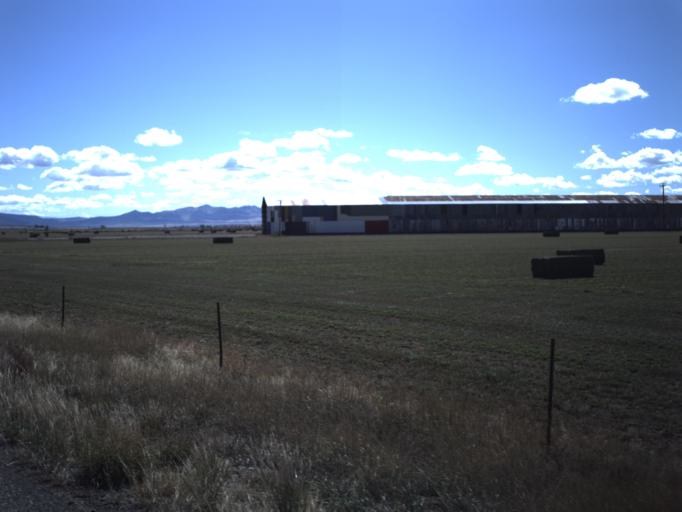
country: US
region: Utah
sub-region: Beaver County
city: Milford
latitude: 38.3552
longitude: -112.9871
